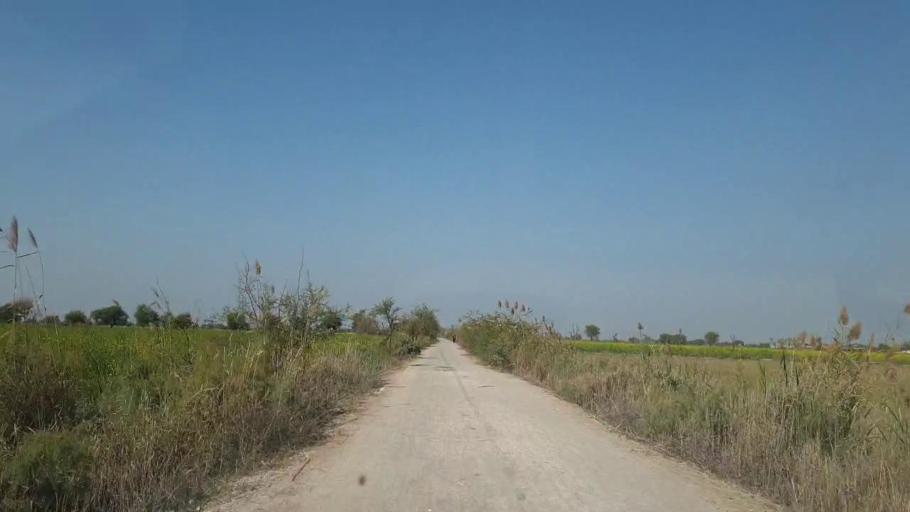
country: PK
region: Sindh
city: Mirpur Khas
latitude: 25.7176
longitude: 69.1393
